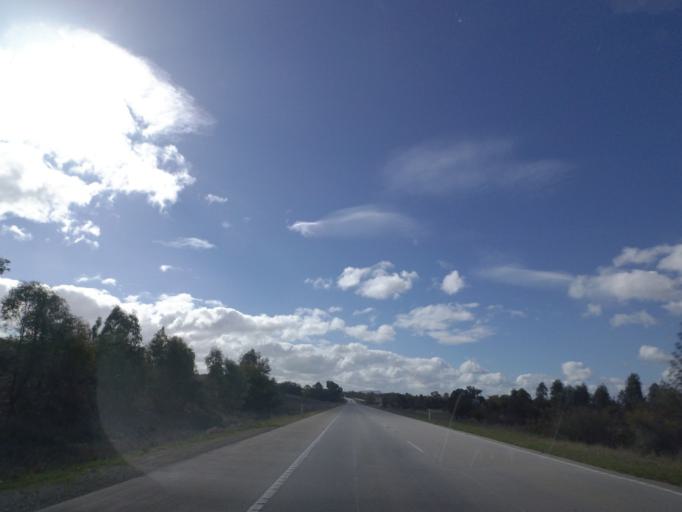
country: AU
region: New South Wales
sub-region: Albury Municipality
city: Lavington
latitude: -36.0090
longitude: 146.9887
